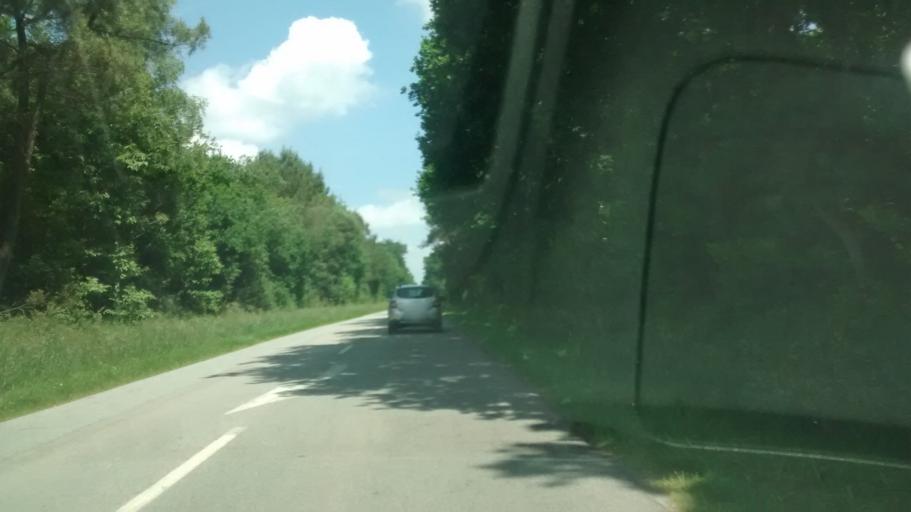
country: FR
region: Brittany
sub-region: Departement du Morbihan
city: Guer
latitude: 47.8768
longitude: -2.1994
